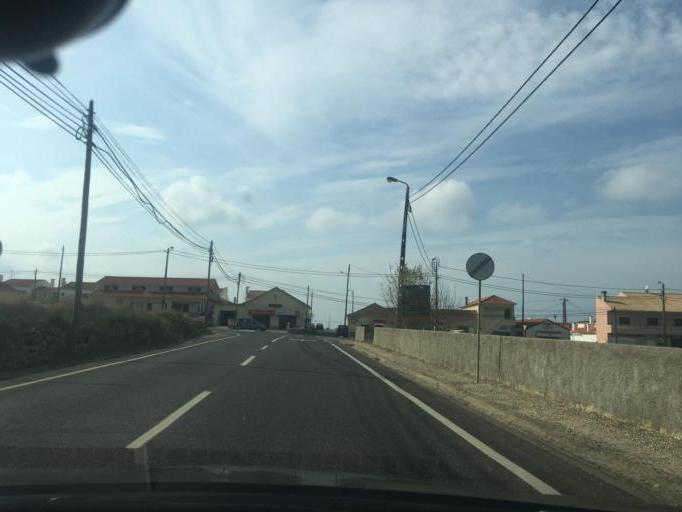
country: PT
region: Lisbon
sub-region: Sintra
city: Sao Joao das Lampas
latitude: 38.8498
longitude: -9.4039
